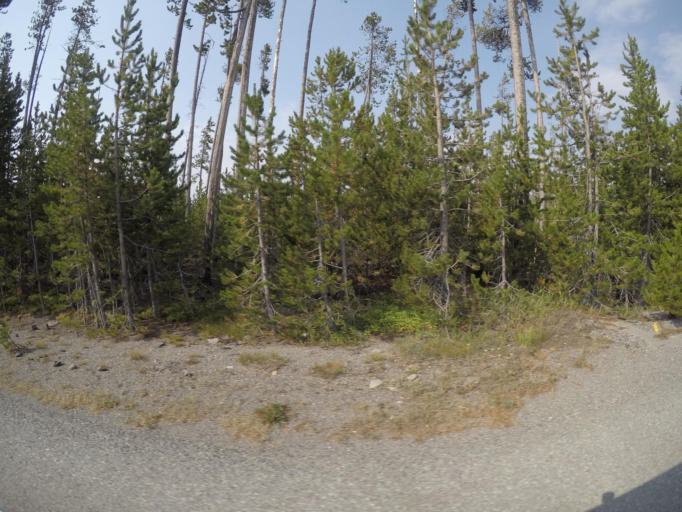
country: US
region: Montana
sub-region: Gallatin County
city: West Yellowstone
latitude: 44.7197
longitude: -110.6490
